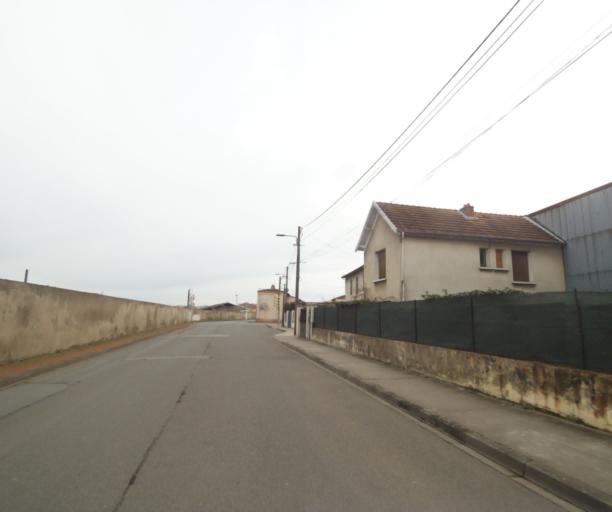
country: FR
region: Rhone-Alpes
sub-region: Departement de la Loire
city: Riorges
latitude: 46.0439
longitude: 4.0602
